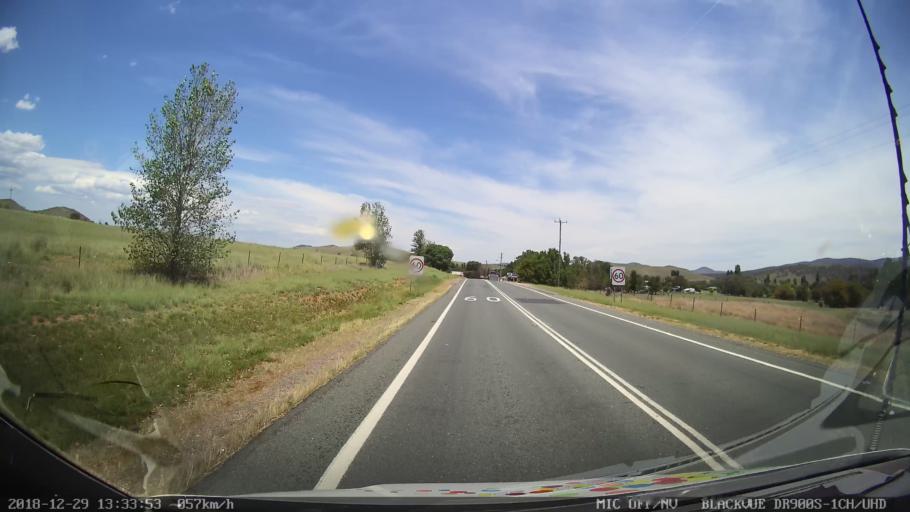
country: AU
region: New South Wales
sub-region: Cooma-Monaro
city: Cooma
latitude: -35.9491
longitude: 149.1459
